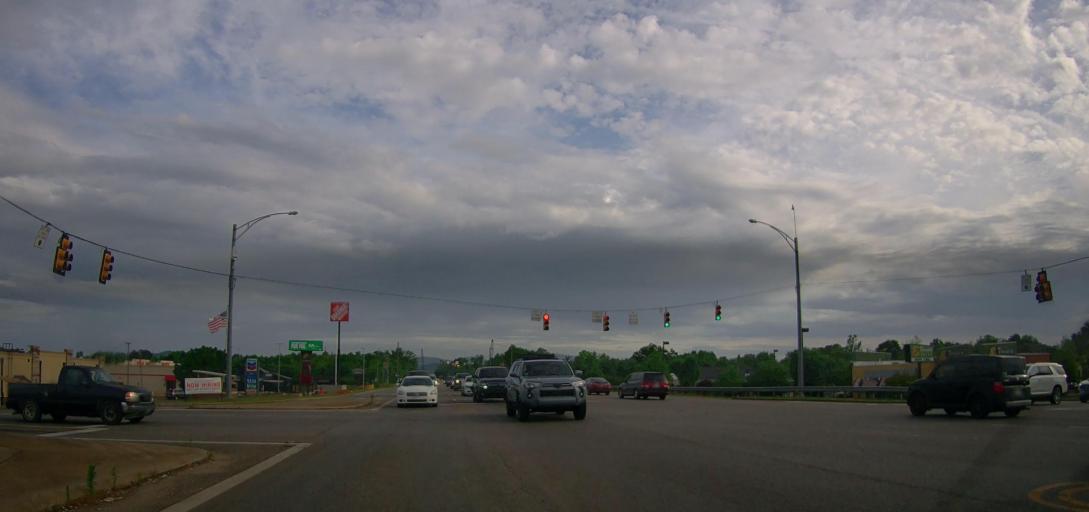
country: US
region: Alabama
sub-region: Calhoun County
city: Oxford
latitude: 33.6095
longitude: -85.7862
